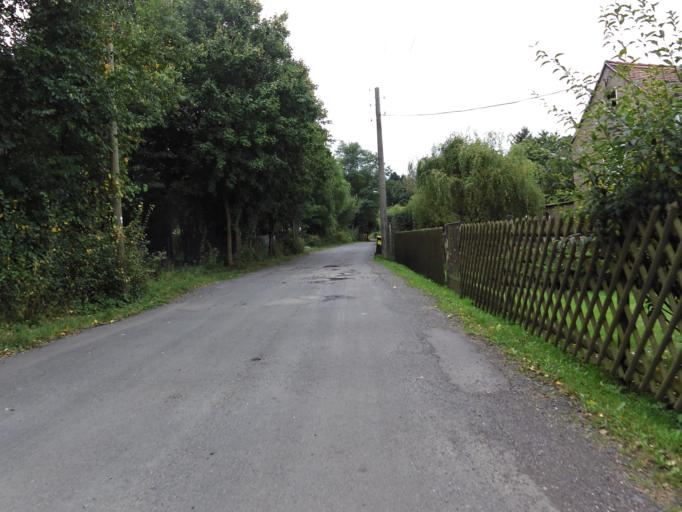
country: DE
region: Saxony
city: Grossposna
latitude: 51.3091
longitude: 12.4629
